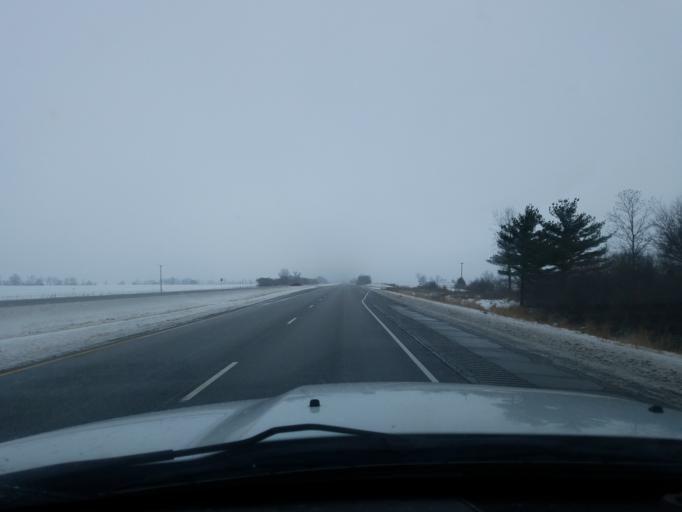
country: US
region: Indiana
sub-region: Fulton County
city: Rochester
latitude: 40.9802
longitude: -86.1679
